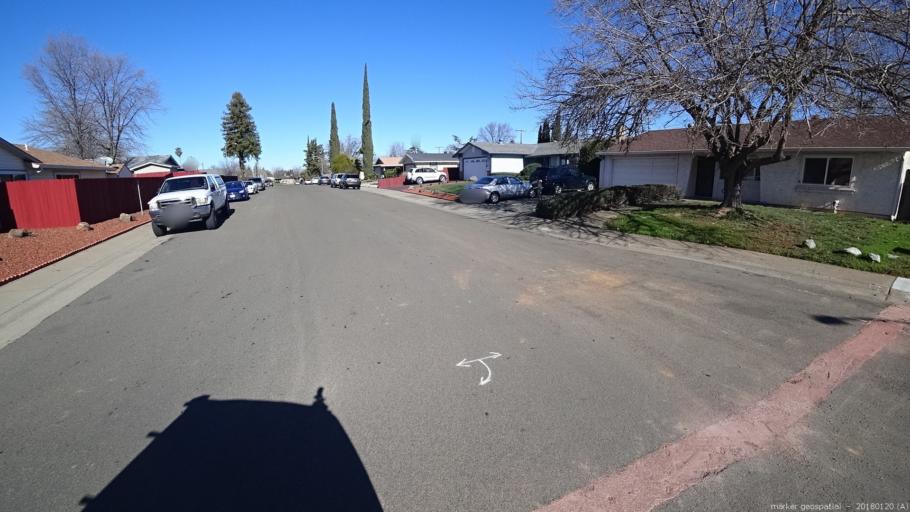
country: US
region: California
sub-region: Sacramento County
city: Rancho Cordova
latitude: 38.5620
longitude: -121.3202
